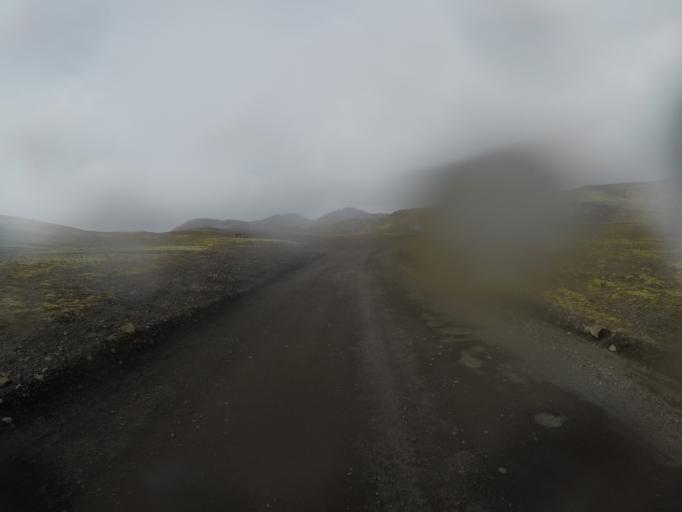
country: IS
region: South
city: Vestmannaeyjar
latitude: 63.9816
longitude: -18.8497
